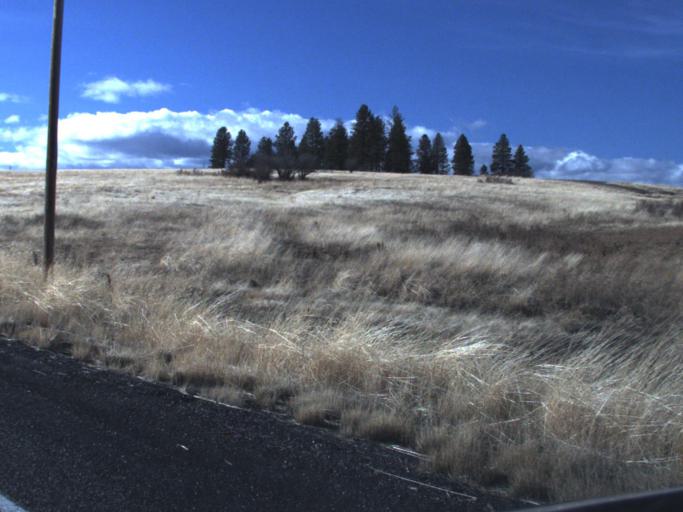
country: US
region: Washington
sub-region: Asotin County
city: Asotin
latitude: 46.1411
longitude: -117.1277
